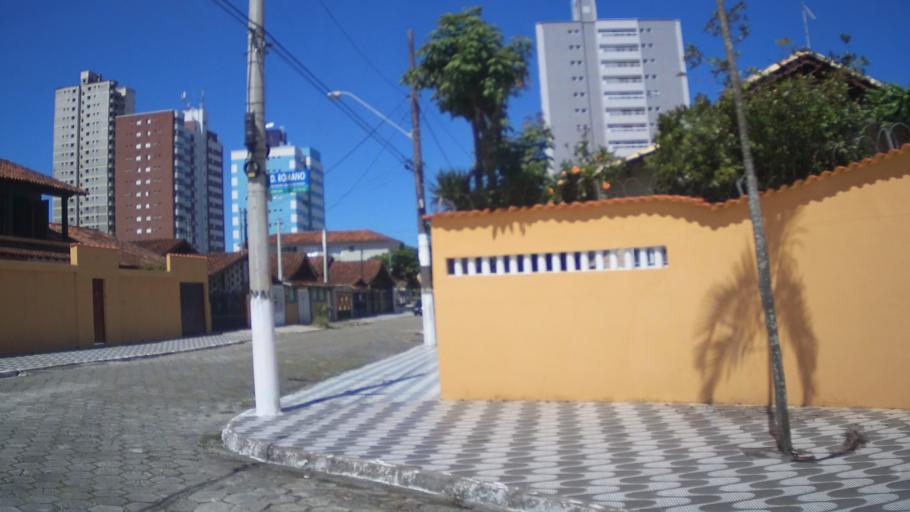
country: BR
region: Sao Paulo
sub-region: Praia Grande
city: Praia Grande
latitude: -24.0403
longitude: -46.5049
